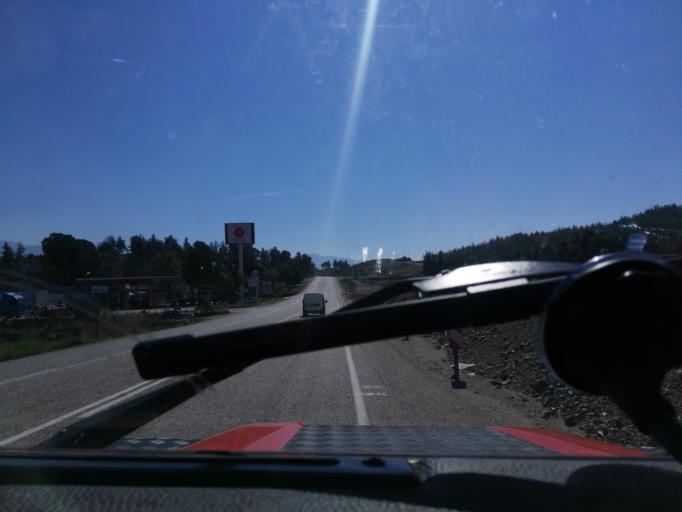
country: TR
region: Mugla
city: Kemer
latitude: 36.6141
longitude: 29.3576
